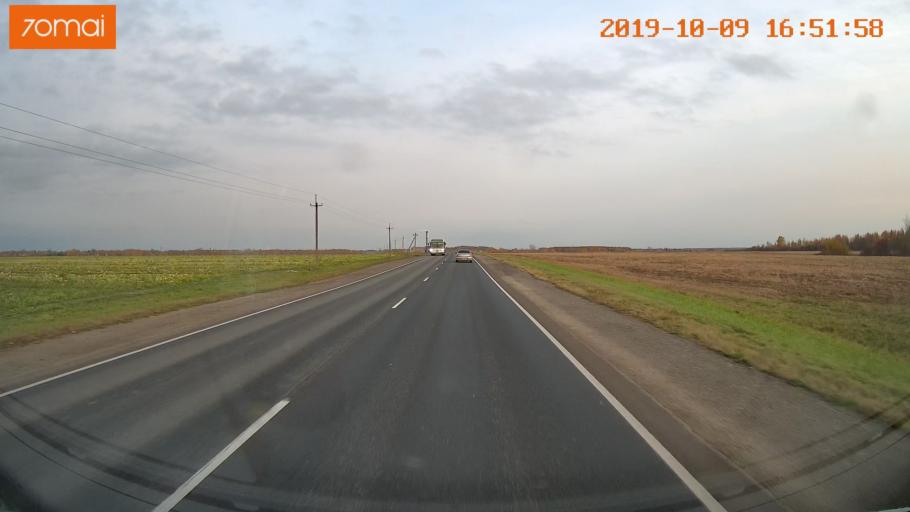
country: RU
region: Ivanovo
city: Privolzhsk
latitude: 57.3833
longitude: 41.2348
